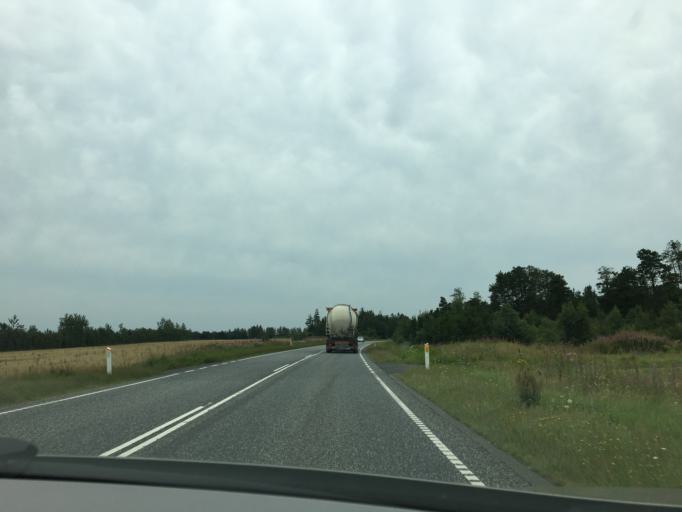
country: DK
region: Central Jutland
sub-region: Herning Kommune
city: Sunds
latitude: 56.3101
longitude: 8.9976
